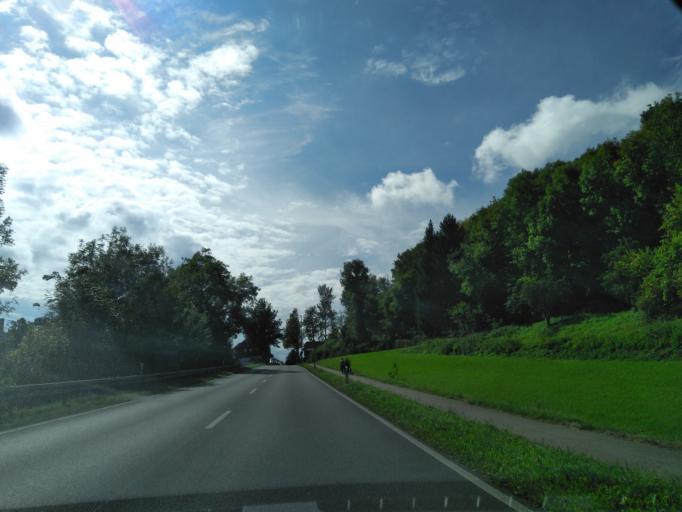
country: DE
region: Baden-Wuerttemberg
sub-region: Regierungsbezirk Stuttgart
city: Besigheim
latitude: 48.9752
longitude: 9.1438
